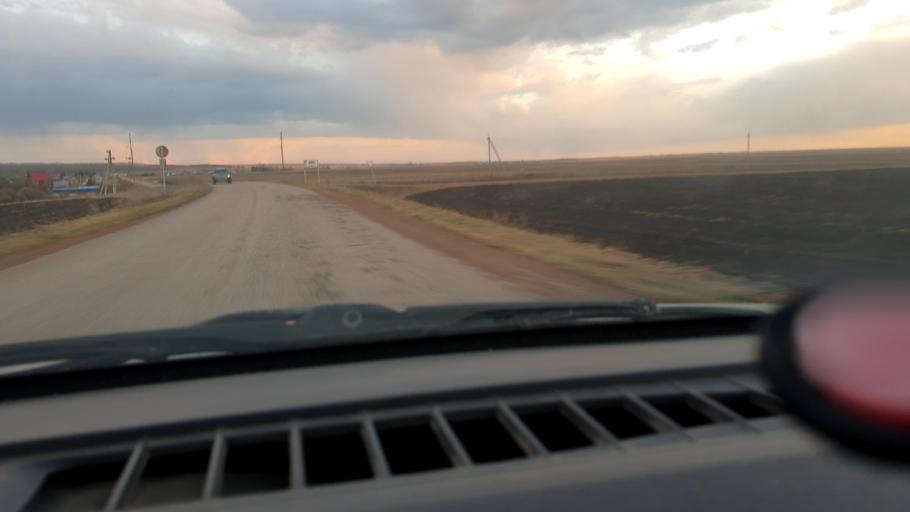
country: RU
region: Bashkortostan
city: Asanovo
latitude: 54.9396
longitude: 55.5171
